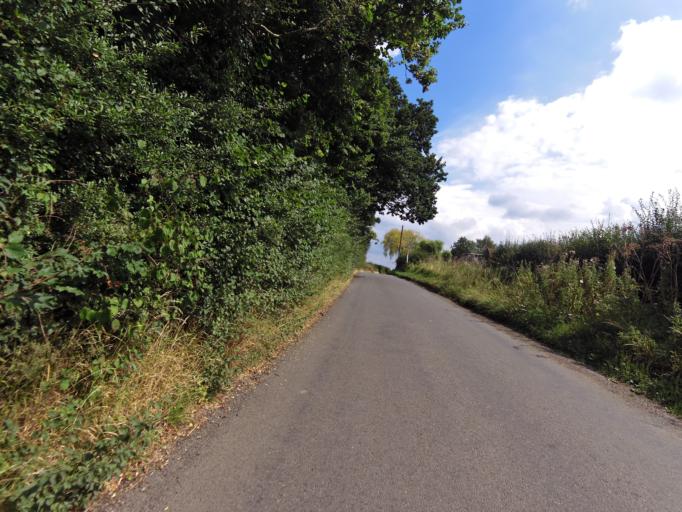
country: GB
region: England
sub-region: Hertfordshire
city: Shenley AV
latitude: 51.6950
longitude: -0.2492
